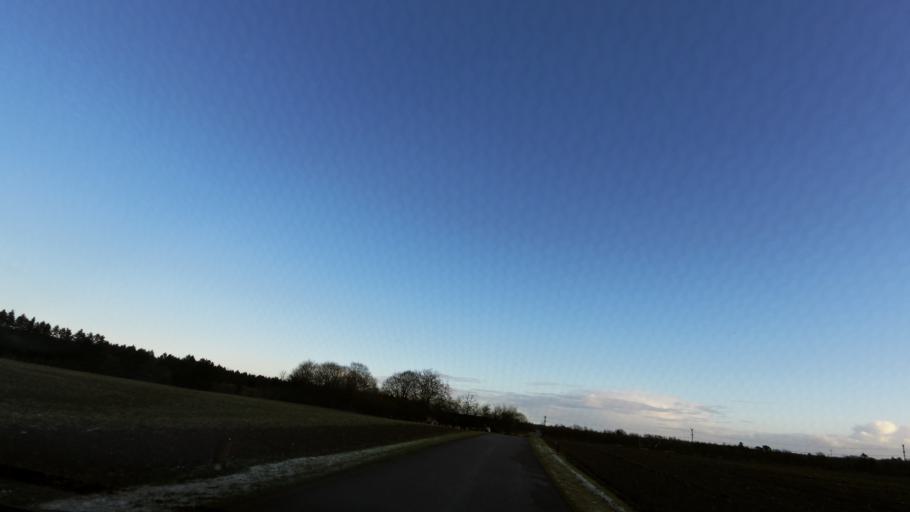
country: DK
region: Central Jutland
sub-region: Ikast-Brande Kommune
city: Ikast
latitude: 56.0275
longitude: 9.2184
